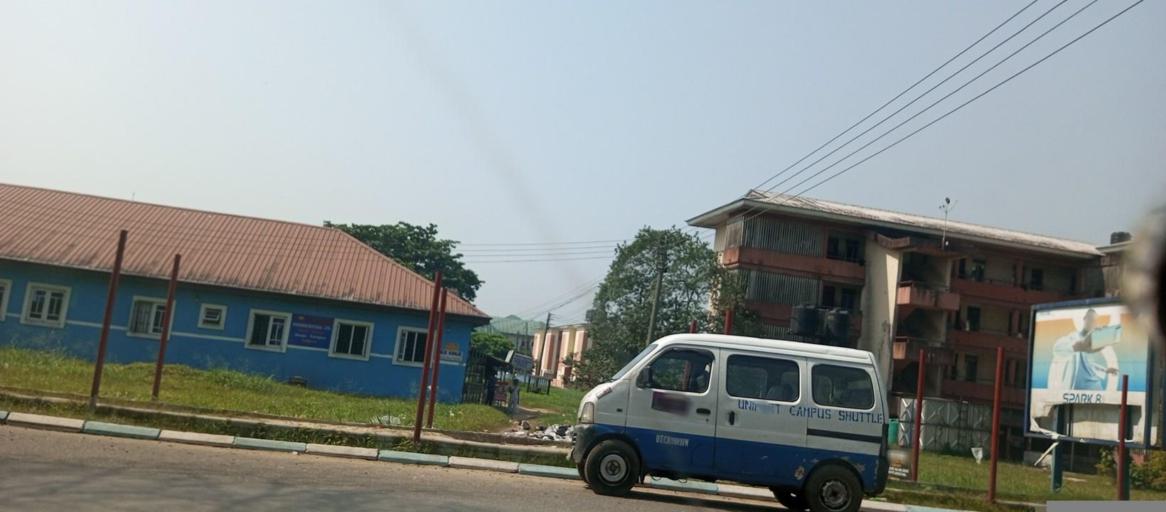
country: NG
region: Rivers
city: Emuoha
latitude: 4.9004
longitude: 6.9247
